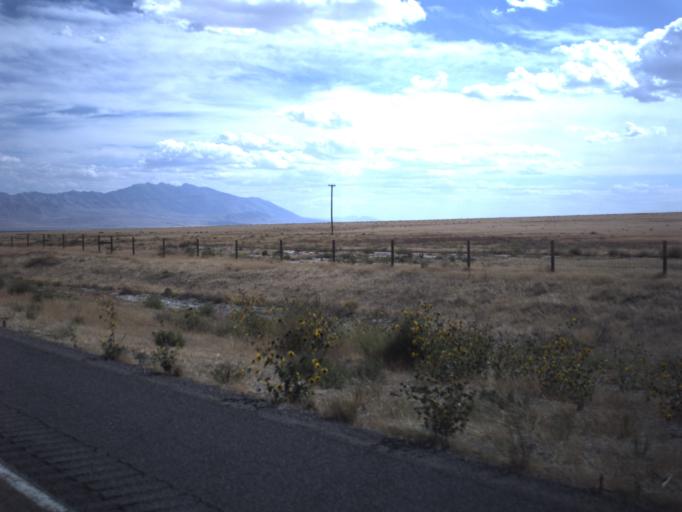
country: US
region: Utah
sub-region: Tooele County
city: Grantsville
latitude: 40.8006
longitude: -112.8508
